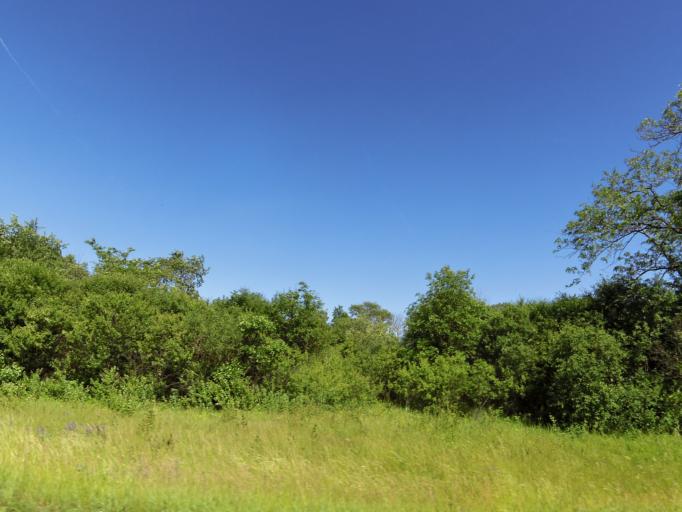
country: US
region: Illinois
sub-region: Ogle County
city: Davis Junction
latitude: 42.1575
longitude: -89.0764
